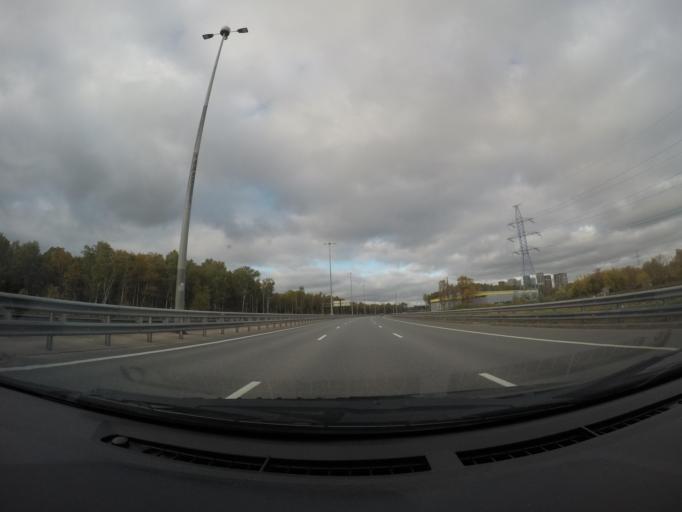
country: RU
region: Moskovskaya
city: Lesnoy Gorodok
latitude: 55.6723
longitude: 37.2247
